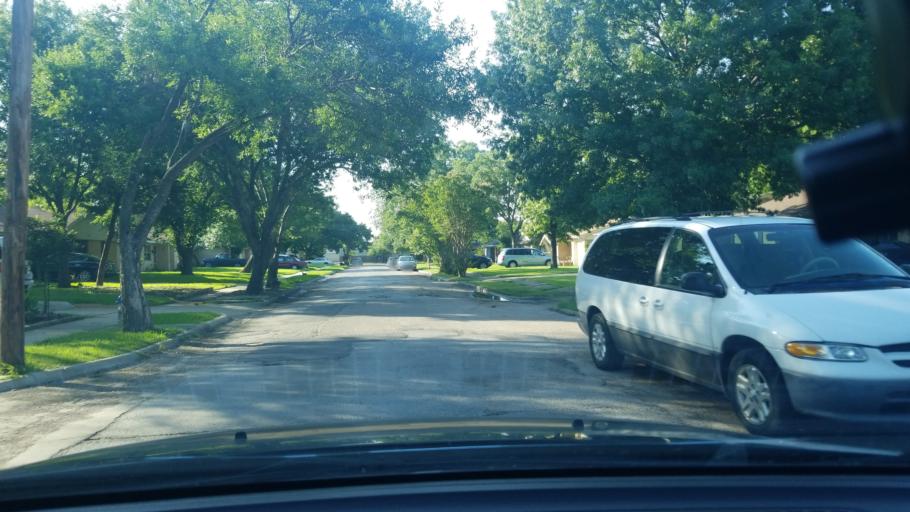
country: US
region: Texas
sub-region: Dallas County
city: Mesquite
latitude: 32.8094
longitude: -96.6396
